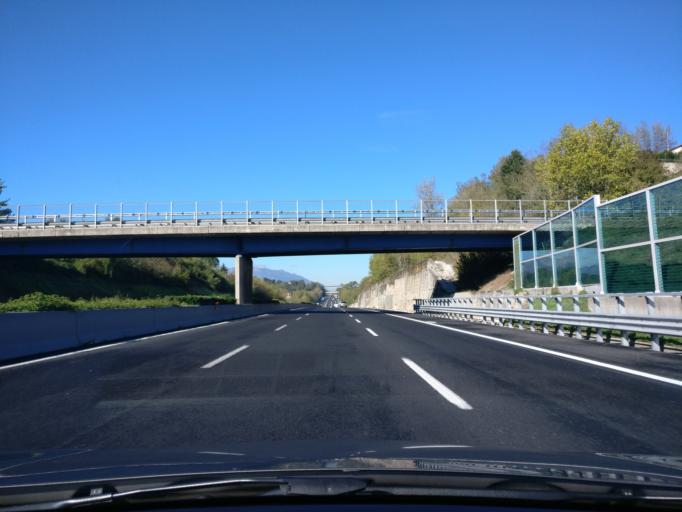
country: IT
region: Latium
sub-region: Provincia di Frosinone
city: Pofi
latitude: 41.5646
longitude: 13.3969
